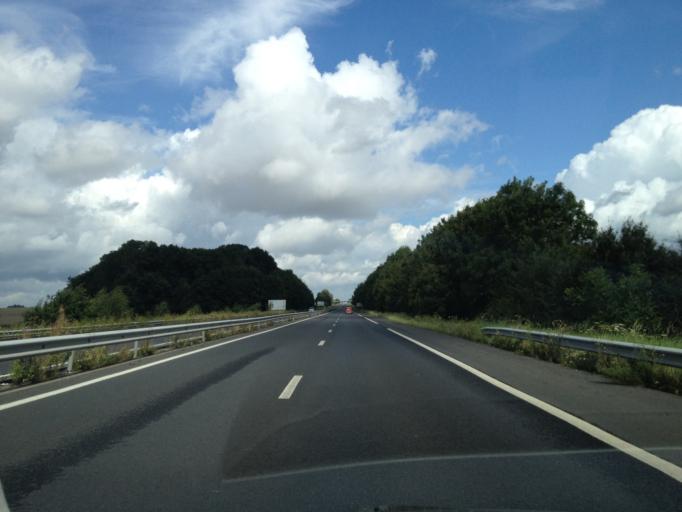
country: FR
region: Haute-Normandie
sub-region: Departement de la Seine-Maritime
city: Saint-Martin-Osmonville
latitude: 49.5985
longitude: 1.2737
